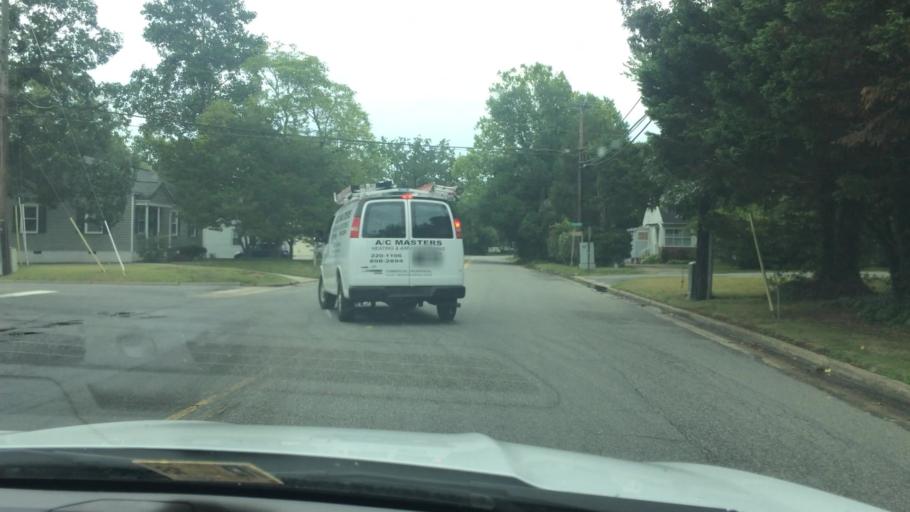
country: US
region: Virginia
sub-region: City of Williamsburg
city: Williamsburg
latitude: 37.2659
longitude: -76.6725
